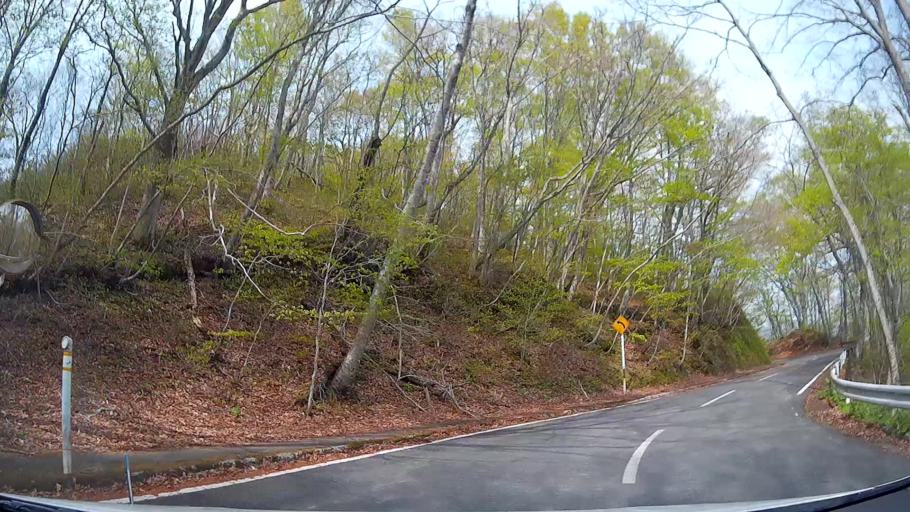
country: JP
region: Akita
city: Hanawa
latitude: 40.4390
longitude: 140.9175
